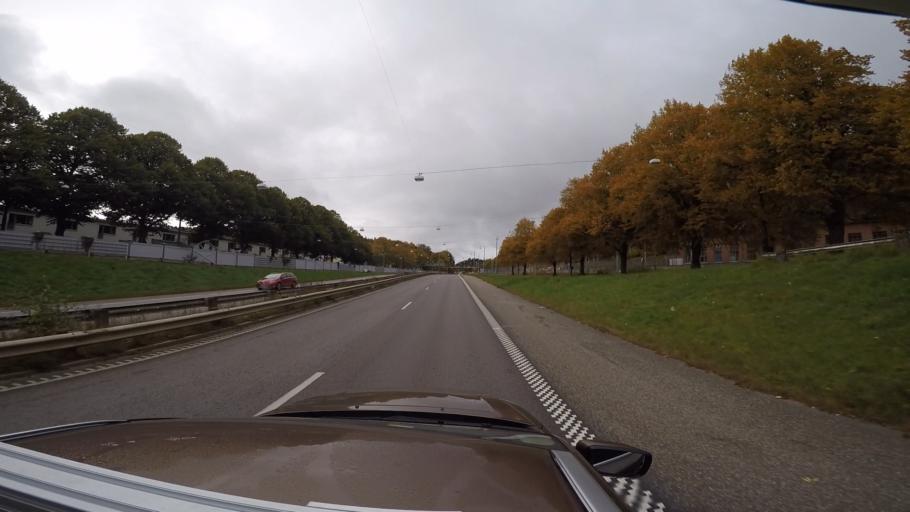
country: SE
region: Vaestra Goetaland
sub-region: Goteborg
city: Majorna
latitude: 57.6801
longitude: 11.9450
